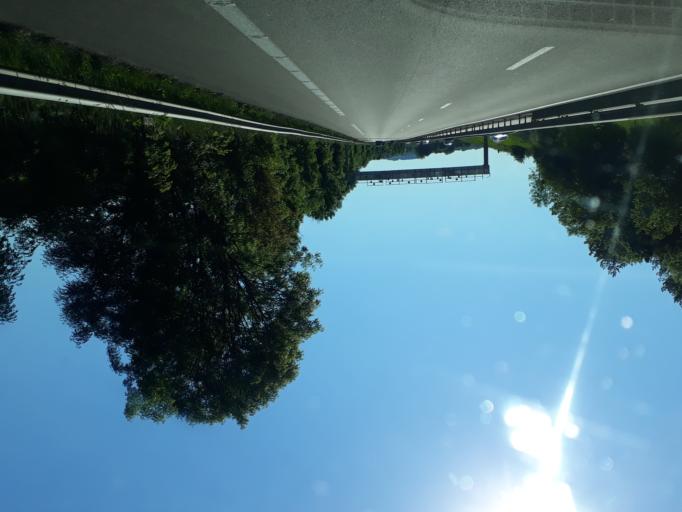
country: FR
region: Bourgogne
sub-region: Departement de la Cote-d'Or
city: Velars-sur-Ouche
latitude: 47.3189
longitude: 4.9240
